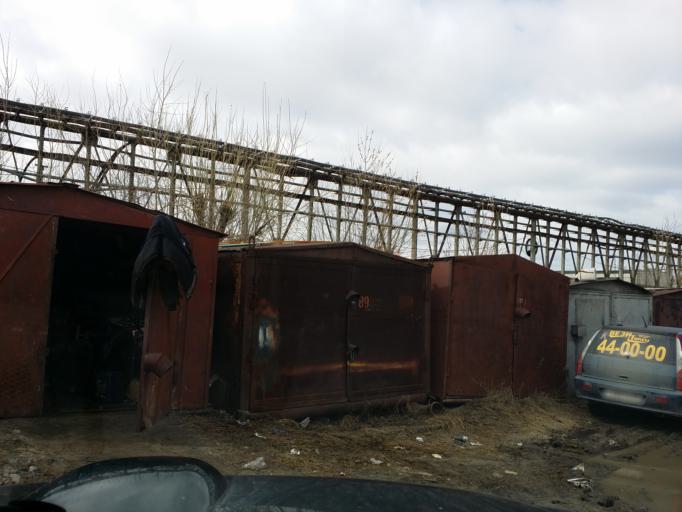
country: RU
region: Khanty-Mansiyskiy Avtonomnyy Okrug
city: Nizhnevartovsk
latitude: 60.9488
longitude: 76.5430
